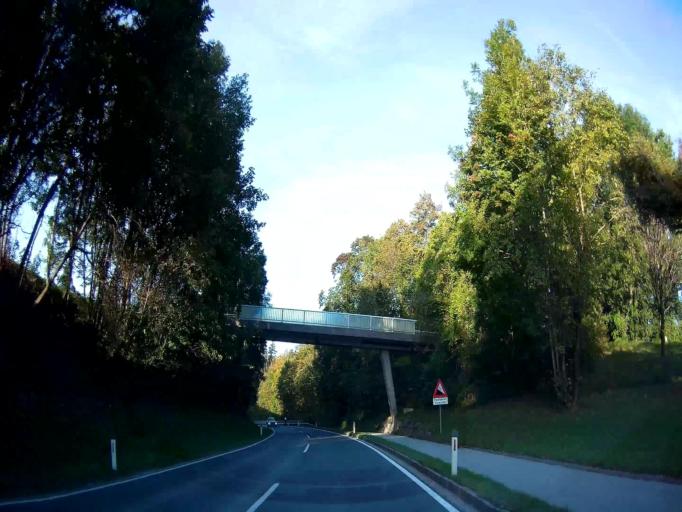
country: DE
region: Bavaria
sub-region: Upper Bavaria
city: Piding
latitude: 47.7405
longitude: 12.9294
